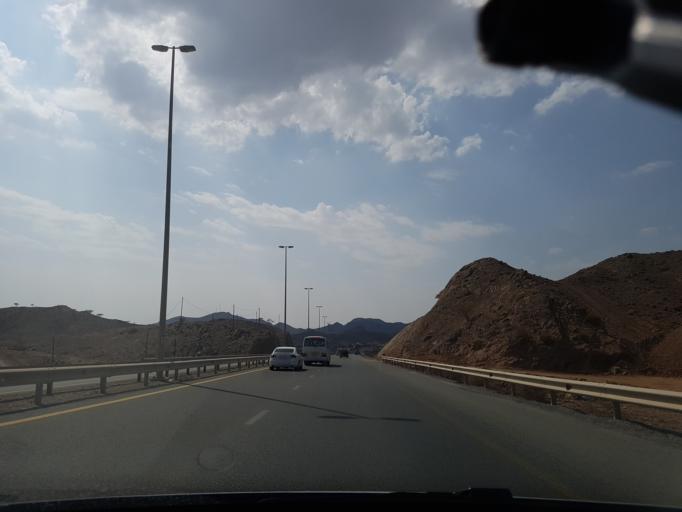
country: AE
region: Al Fujayrah
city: Dibba Al-Fujairah
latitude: 25.5153
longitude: 56.0819
